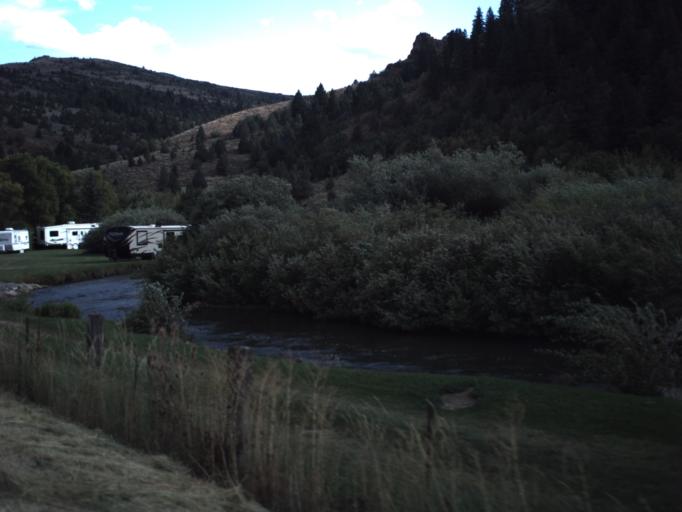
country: US
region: Utah
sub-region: Cache County
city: Millville
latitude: 41.6156
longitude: -111.6381
